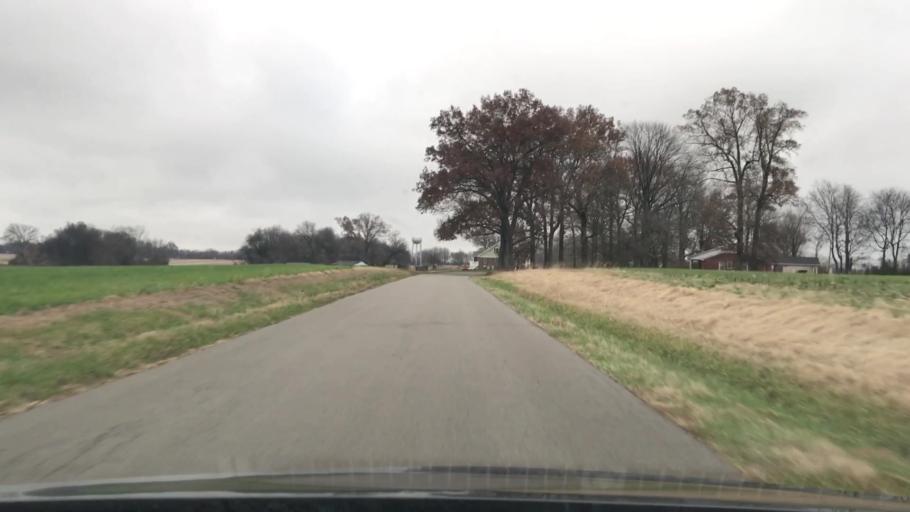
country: US
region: Kentucky
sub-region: Todd County
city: Elkton
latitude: 36.7893
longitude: -87.1511
